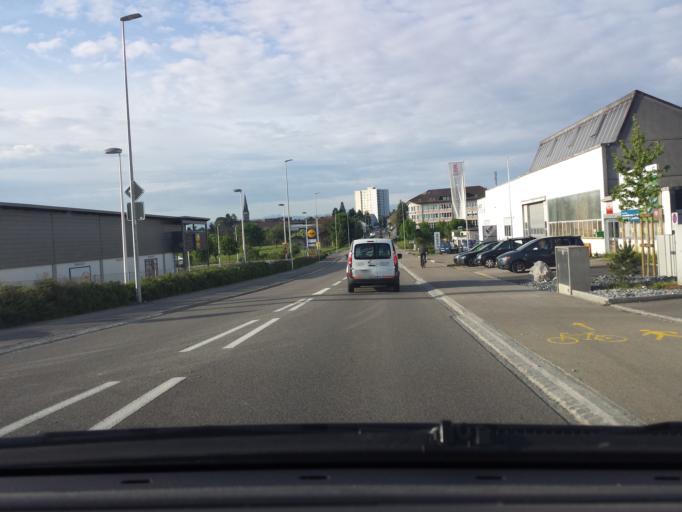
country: CH
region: Thurgau
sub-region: Arbon District
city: Romanshorn
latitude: 47.5722
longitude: 9.3658
